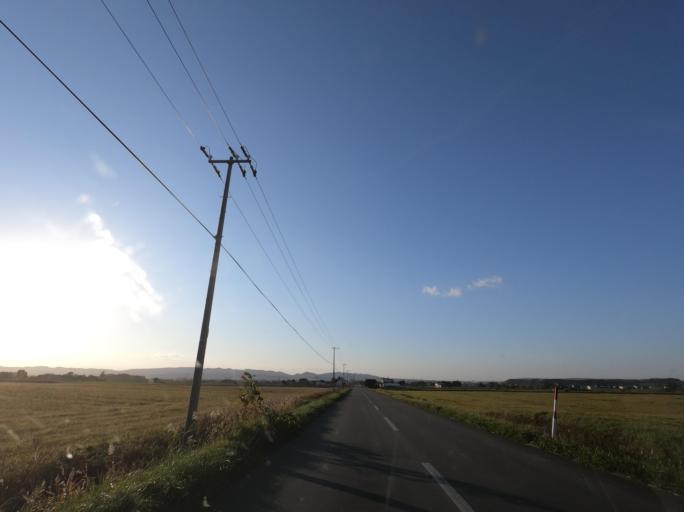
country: JP
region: Hokkaido
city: Iwamizawa
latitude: 42.9970
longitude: 141.8727
